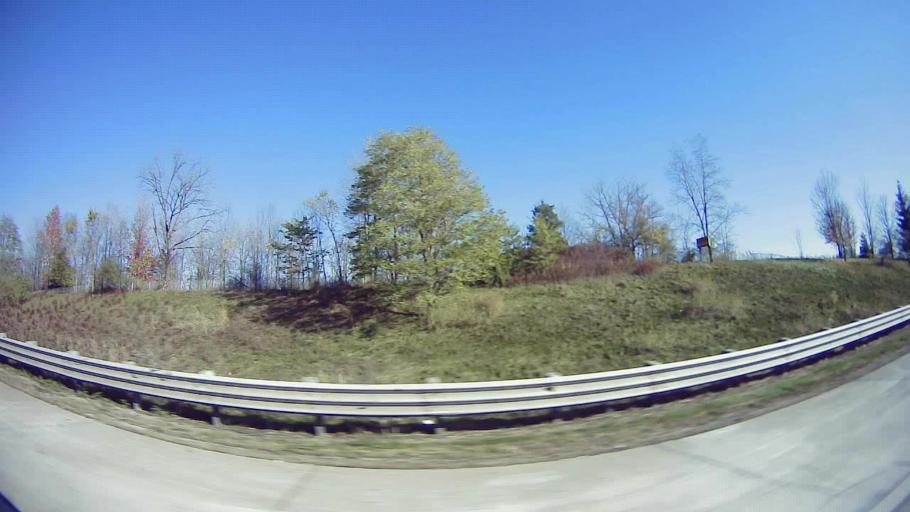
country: US
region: Michigan
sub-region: Oakland County
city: Walled Lake
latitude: 42.5222
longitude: -83.4456
